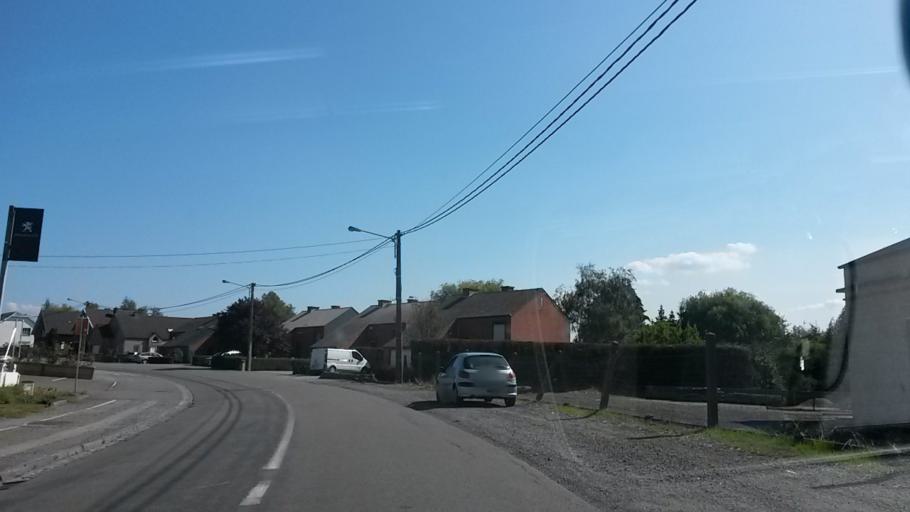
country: BE
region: Wallonia
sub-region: Province du Hainaut
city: Merbes-le-Chateau
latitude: 50.3261
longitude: 4.1716
